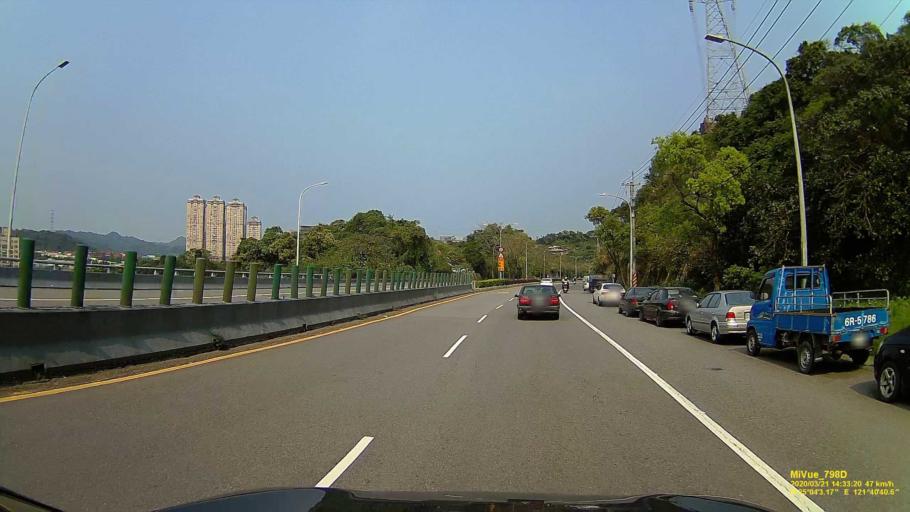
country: TW
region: Taiwan
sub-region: Keelung
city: Keelung
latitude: 25.0677
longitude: 121.6782
